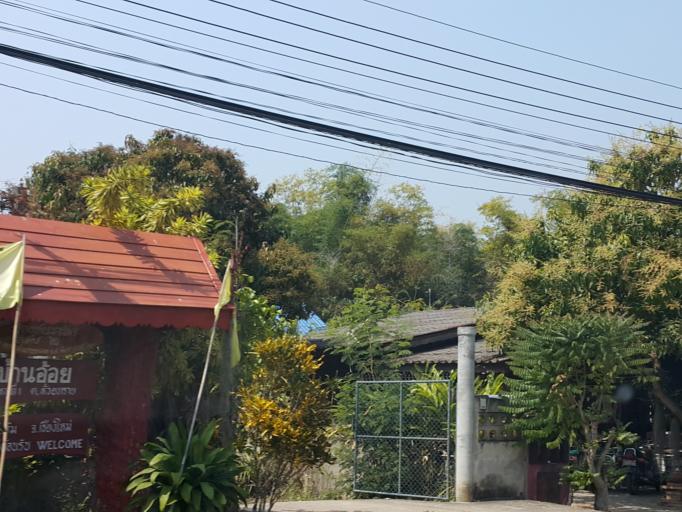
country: TH
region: Chiang Mai
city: San Sai
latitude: 18.9416
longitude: 98.9226
